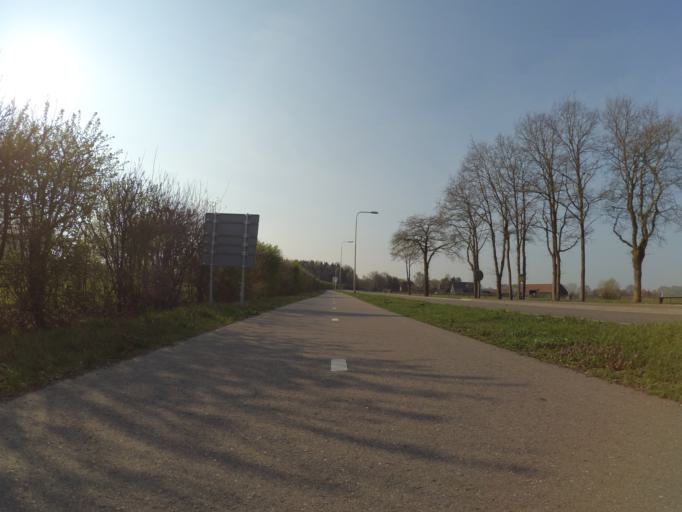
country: NL
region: Gelderland
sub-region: Gemeente Putten
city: Putten
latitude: 52.2376
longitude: 5.6098
